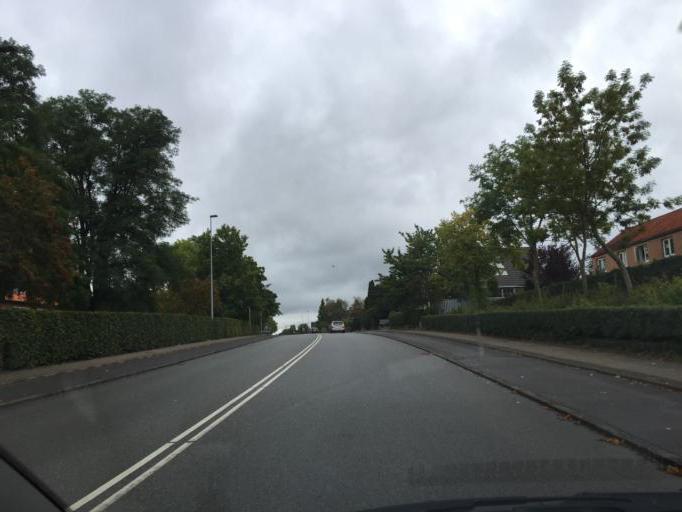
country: DK
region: Capital Region
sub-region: Gladsaxe Municipality
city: Buddinge
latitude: 55.7423
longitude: 12.4723
